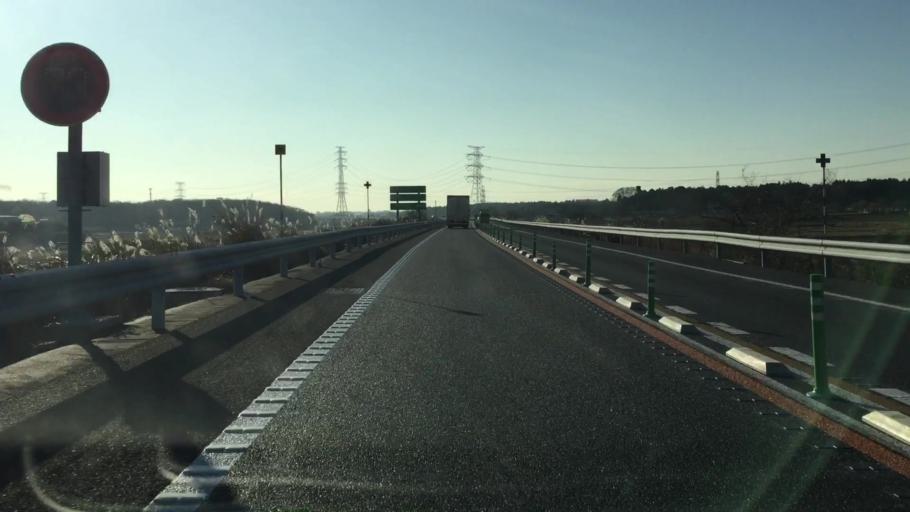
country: JP
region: Ibaraki
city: Naka
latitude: 36.0133
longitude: 140.1424
